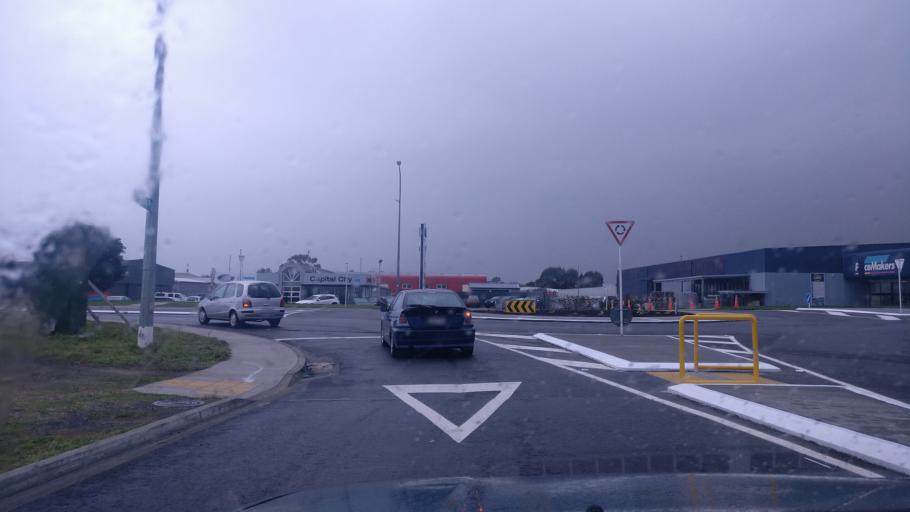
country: NZ
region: Wellington
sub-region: Kapiti Coast District
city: Paraparaumu
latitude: -40.9040
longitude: 174.9945
